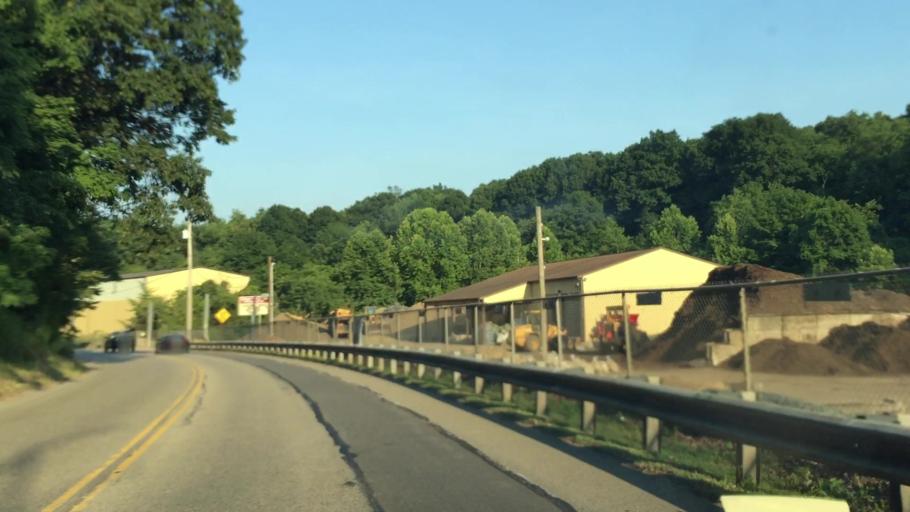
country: US
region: Pennsylvania
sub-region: Allegheny County
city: South Park Township
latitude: 40.2875
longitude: -80.0031
